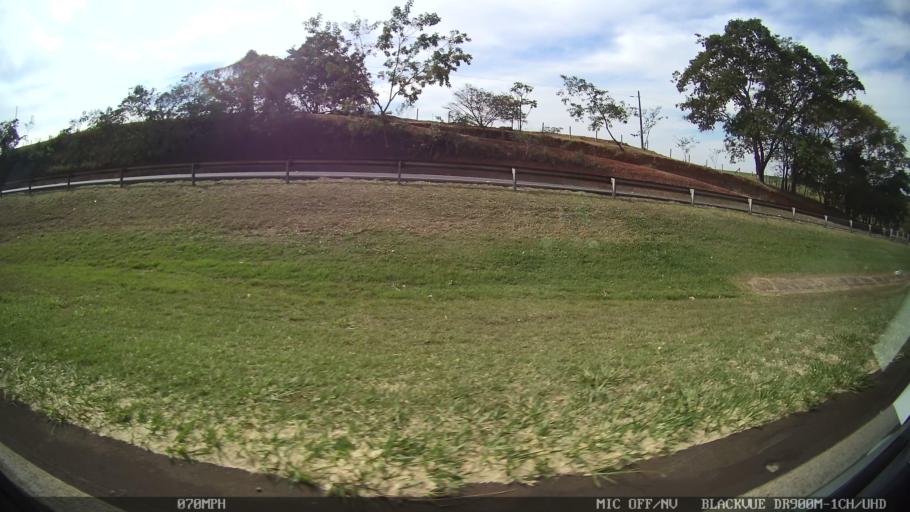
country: BR
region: Sao Paulo
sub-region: Matao
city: Matao
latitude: -21.6004
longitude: -48.4332
